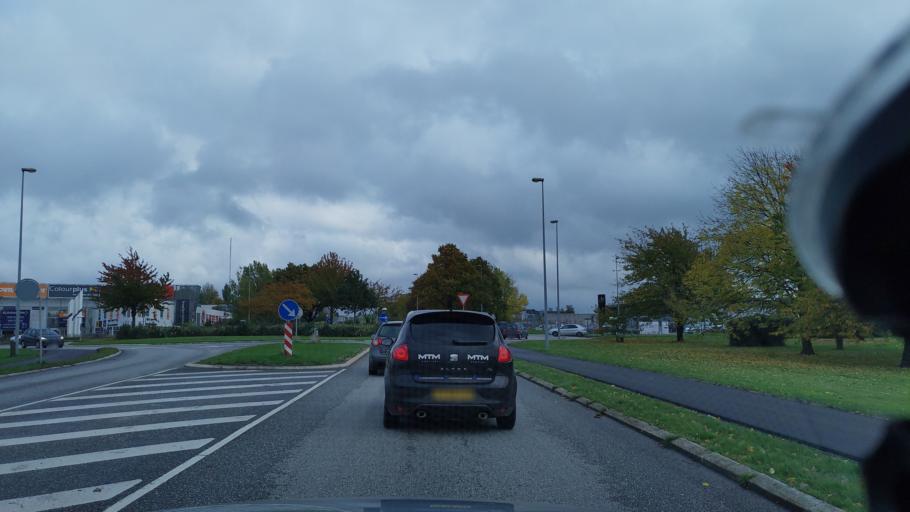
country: DK
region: Zealand
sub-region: Naestved Kommune
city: Fensmark
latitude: 55.2522
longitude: 11.7861
